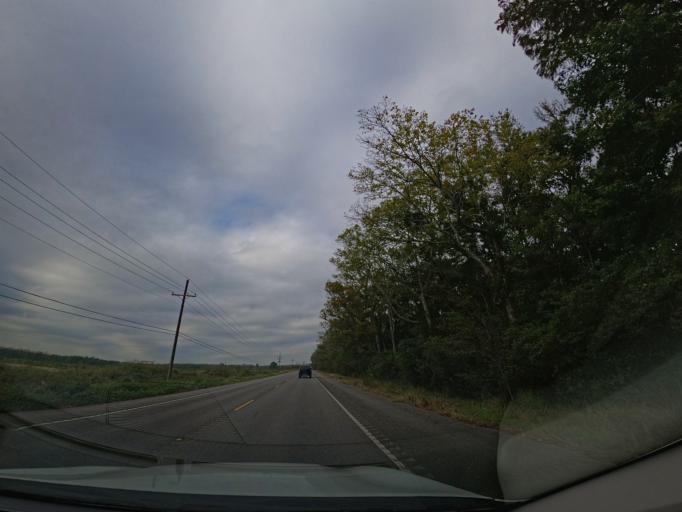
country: US
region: Louisiana
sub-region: Saint Mary Parish
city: Amelia
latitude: 29.6664
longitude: -91.0336
